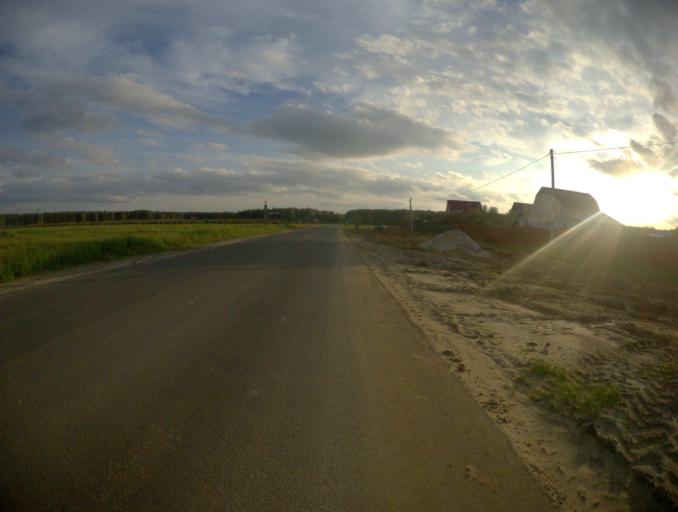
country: RU
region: Vladimir
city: Anopino
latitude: 55.6347
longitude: 40.8011
